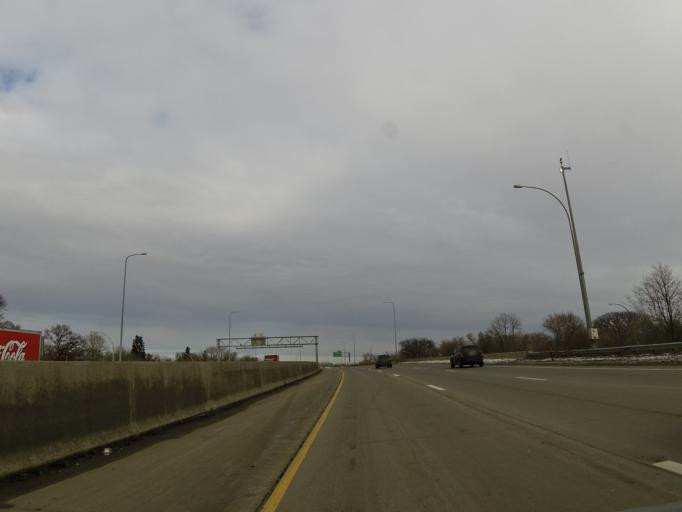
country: US
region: Minnesota
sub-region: Hennepin County
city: Richfield
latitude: 44.8820
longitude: -93.2962
